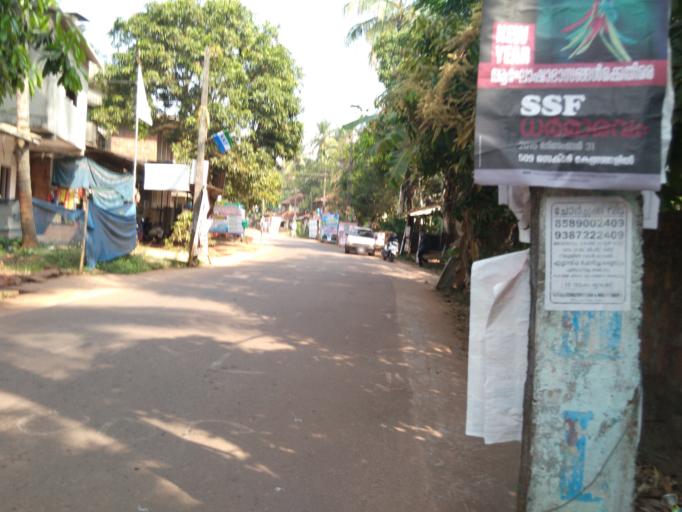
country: IN
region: Kerala
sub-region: Kozhikode
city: Kunnamangalam
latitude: 11.2909
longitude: 75.8363
